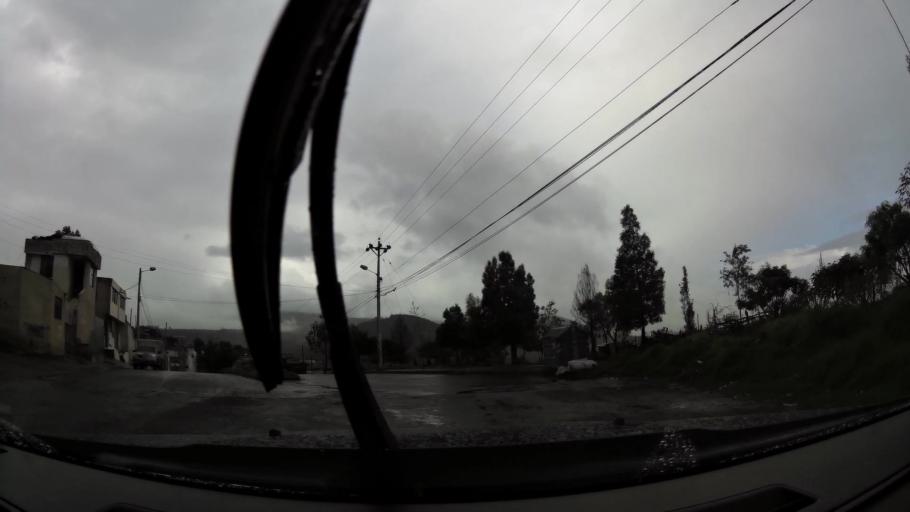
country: EC
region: Pichincha
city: Quito
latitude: -0.0916
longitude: -78.5121
